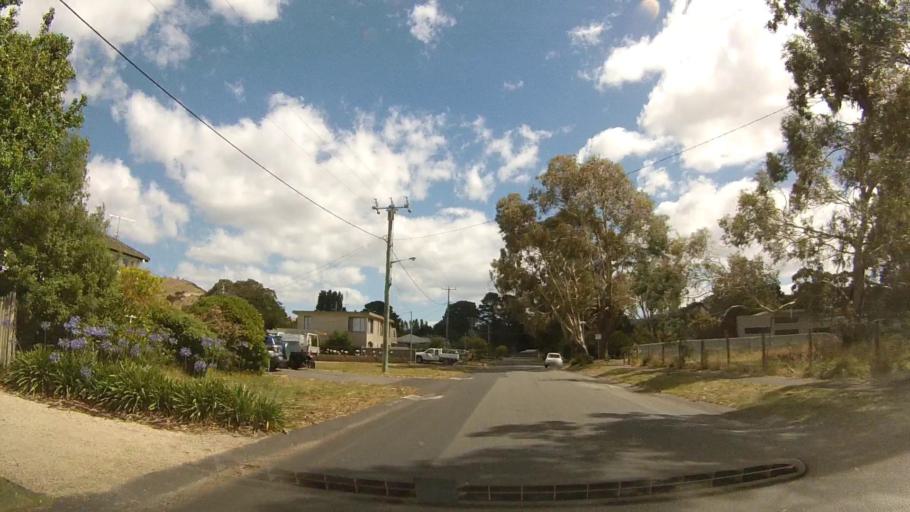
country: AU
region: Tasmania
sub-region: Clarence
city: Seven Mile Beach
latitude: -42.8580
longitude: 147.5022
